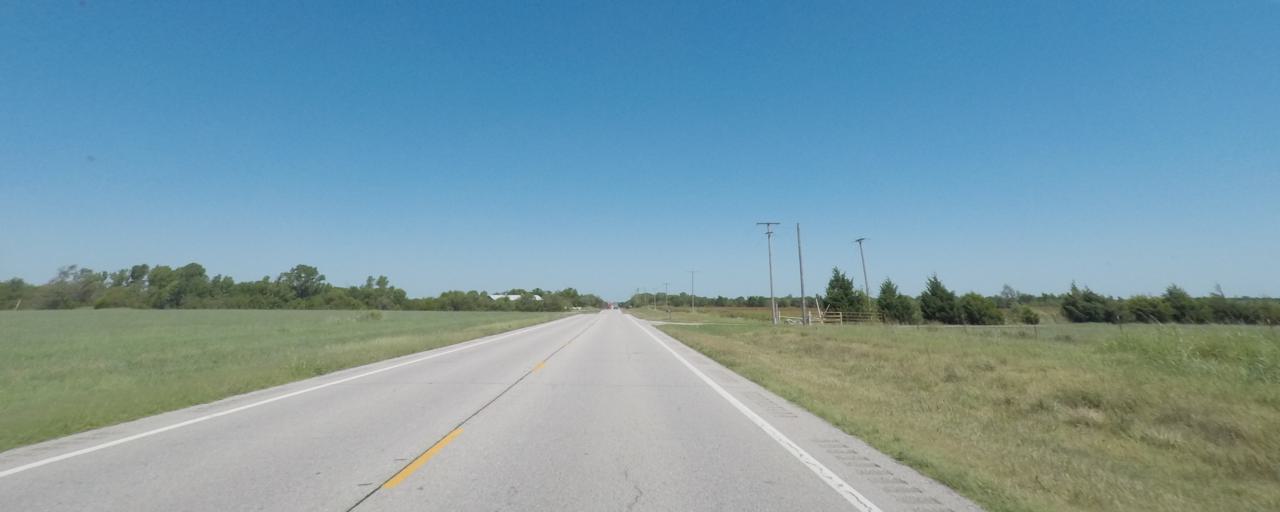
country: US
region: Kansas
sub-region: Sumner County
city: Wellington
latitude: 37.3668
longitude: -97.3850
